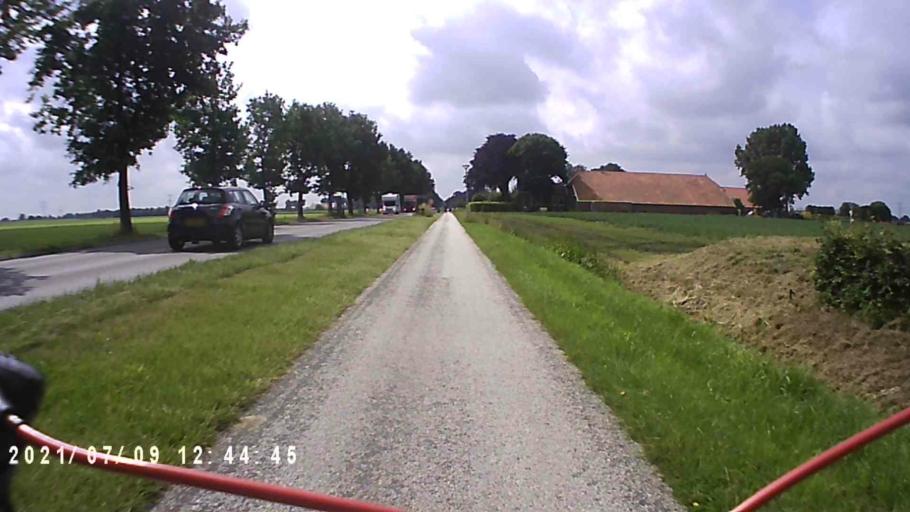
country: NL
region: Groningen
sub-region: Gemeente  Oldambt
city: Winschoten
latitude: 53.1315
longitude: 7.0231
